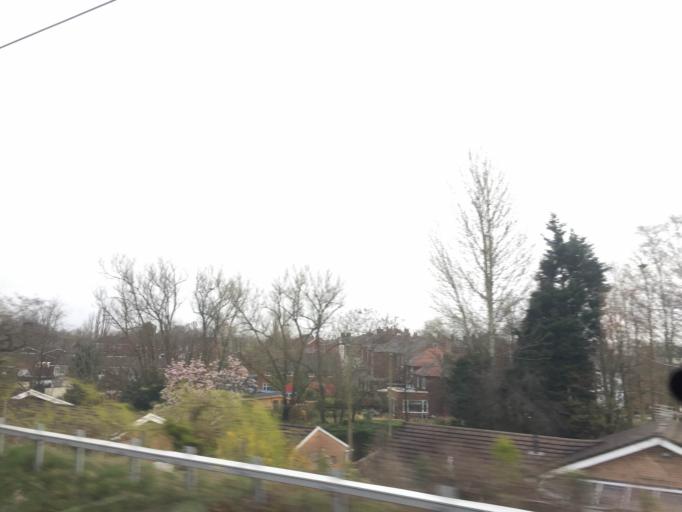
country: GB
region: England
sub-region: Lancashire
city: Coppull
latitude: 53.6247
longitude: -2.6596
